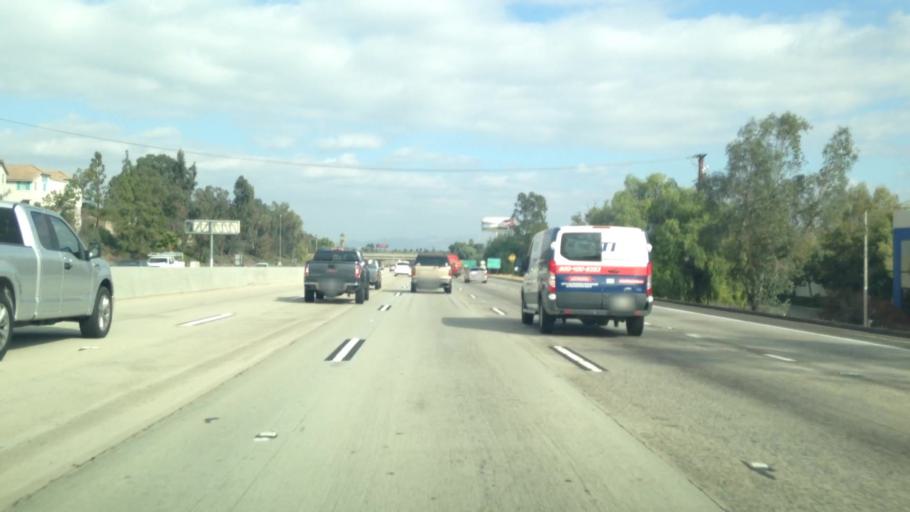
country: US
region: California
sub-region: Riverside County
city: Home Gardens
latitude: 33.8921
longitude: -117.5054
